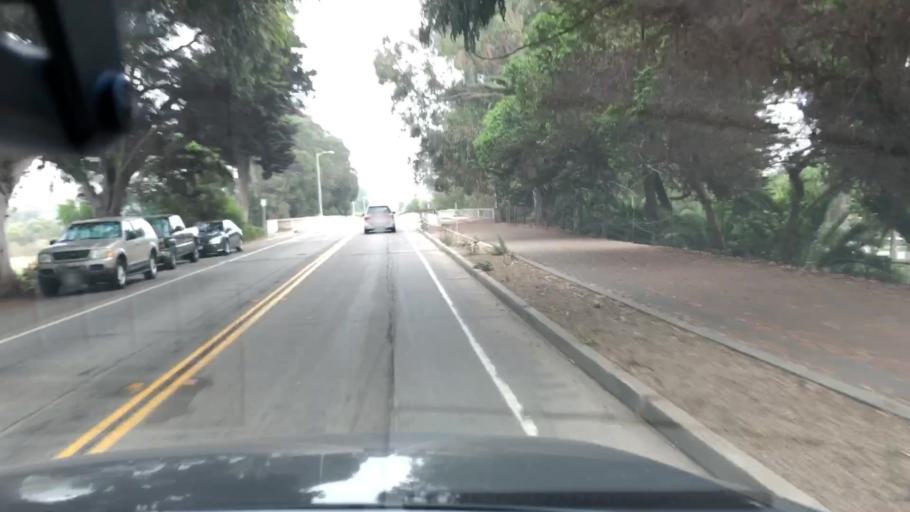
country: US
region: California
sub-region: Ventura County
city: Ventura
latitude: 34.2823
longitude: -119.3112
